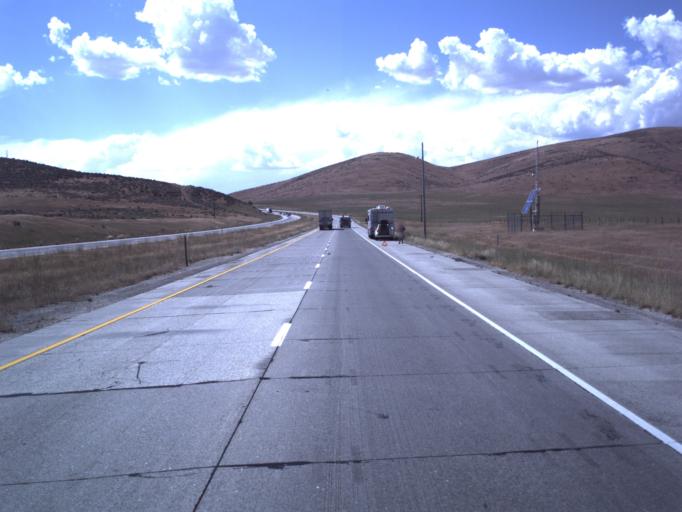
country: US
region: Utah
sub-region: Box Elder County
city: Garland
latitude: 41.8095
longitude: -112.3385
